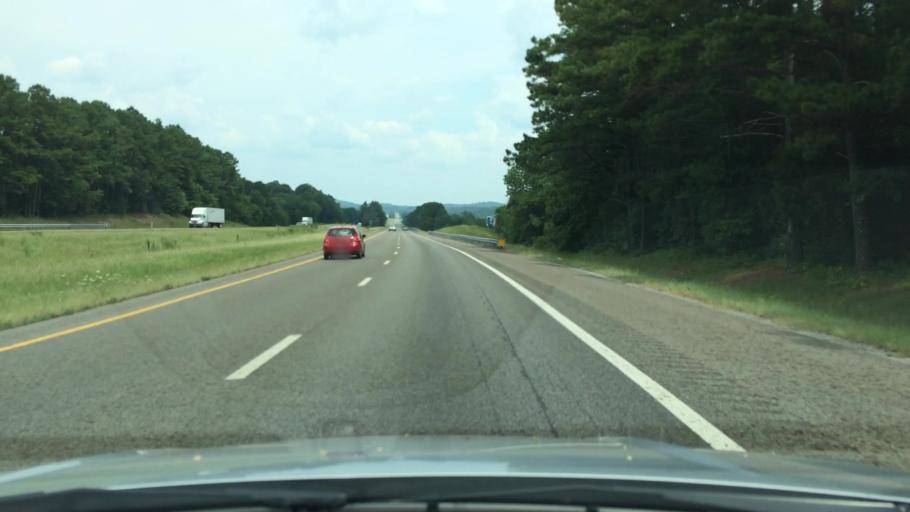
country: US
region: Tennessee
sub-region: Marshall County
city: Cornersville
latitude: 35.4167
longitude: -86.8766
